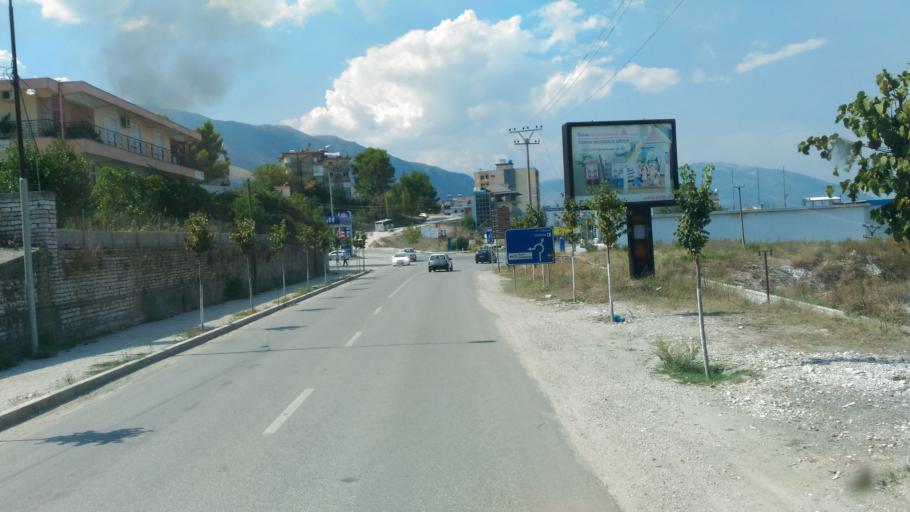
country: AL
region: Gjirokaster
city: Gjirokaster
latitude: 40.0768
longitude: 20.1521
